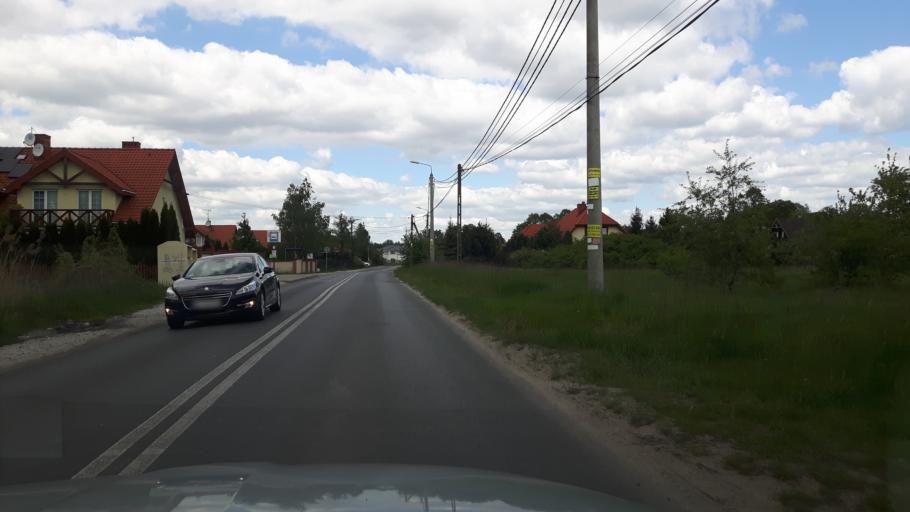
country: PL
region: Masovian Voivodeship
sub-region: Powiat legionowski
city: Stanislawow Pierwszy
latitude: 52.3347
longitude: 21.0541
